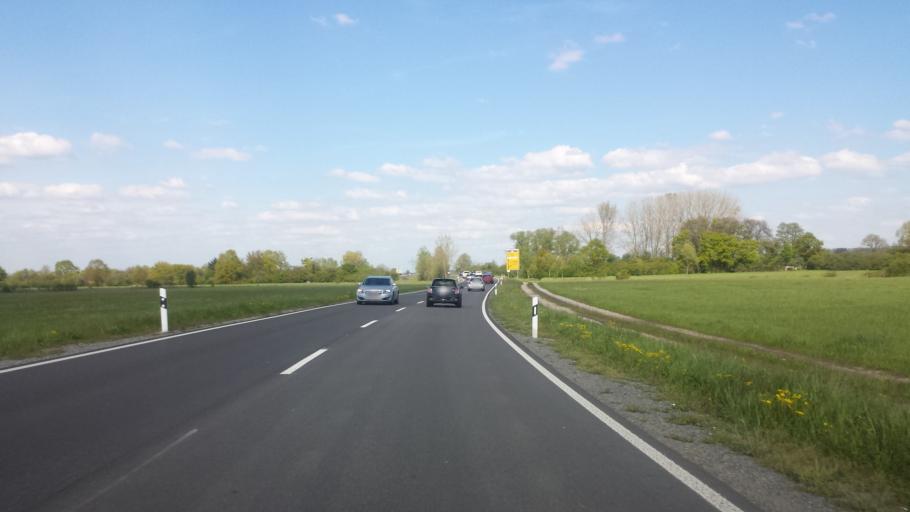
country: DE
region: Baden-Wuerttemberg
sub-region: Karlsruhe Region
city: Weingarten
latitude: 49.0934
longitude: 8.4862
